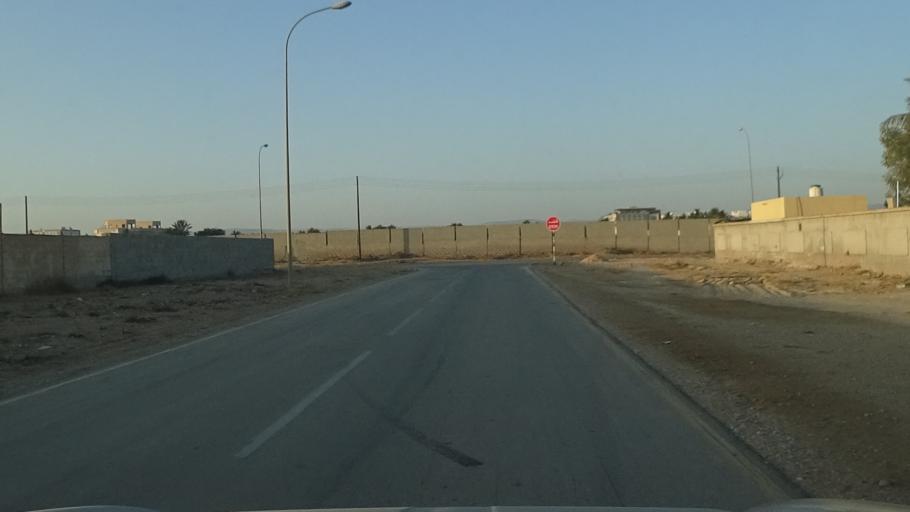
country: OM
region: Zufar
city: Salalah
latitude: 17.0304
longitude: 54.1691
